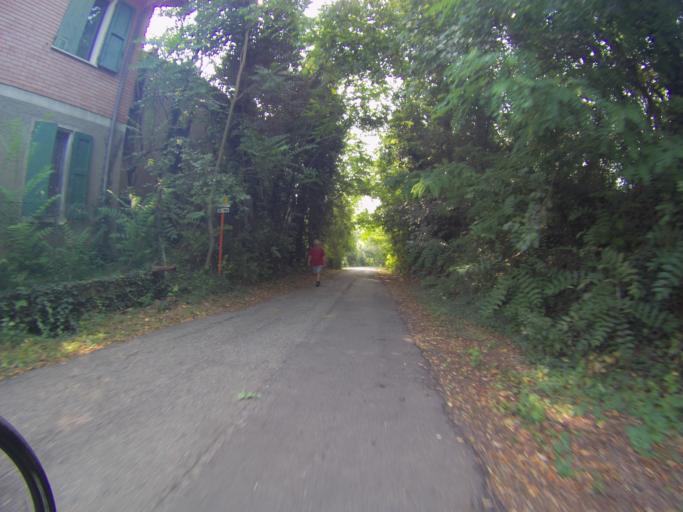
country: IT
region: Emilia-Romagna
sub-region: Provincia di Reggio Emilia
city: Borzano
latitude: 44.6132
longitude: 10.6288
